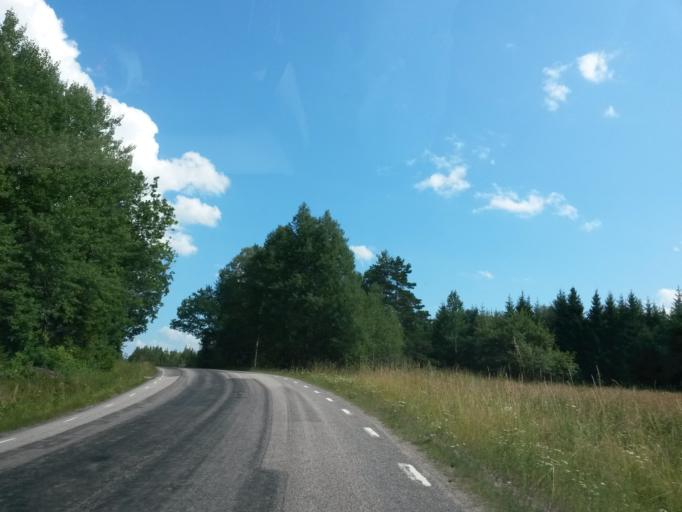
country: SE
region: Vaestra Goetaland
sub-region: Vargarda Kommun
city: Vargarda
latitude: 58.1027
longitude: 12.8139
